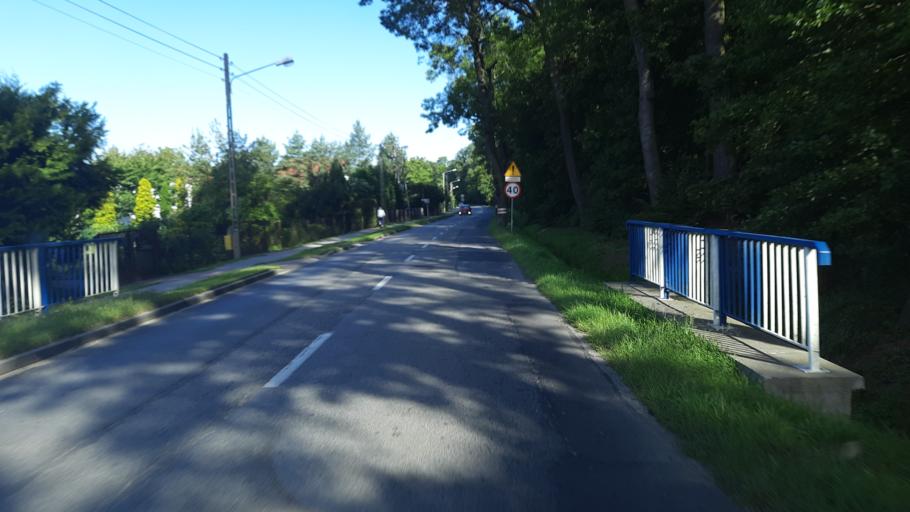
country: PL
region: Lower Silesian Voivodeship
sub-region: Powiat wroclawski
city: Dlugoleka
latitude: 51.1812
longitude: 17.1896
